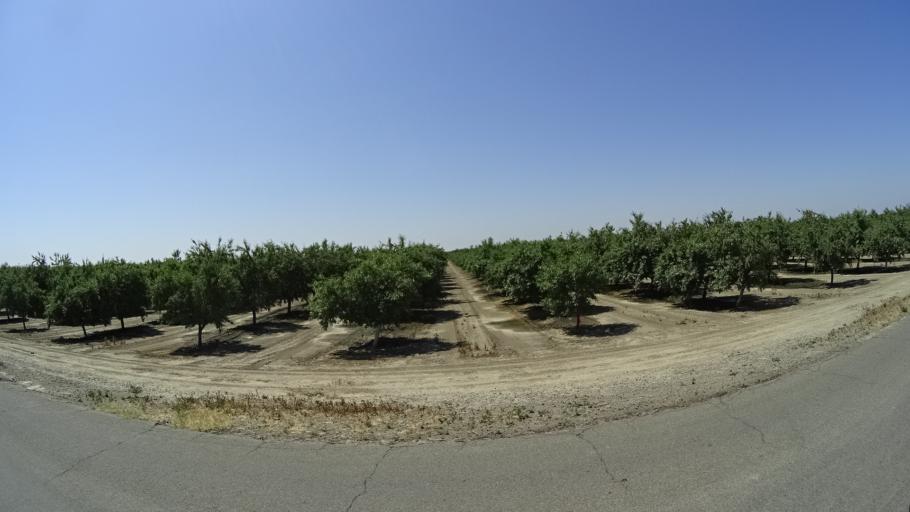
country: US
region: California
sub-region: Kings County
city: Lucerne
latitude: 36.3718
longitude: -119.7162
